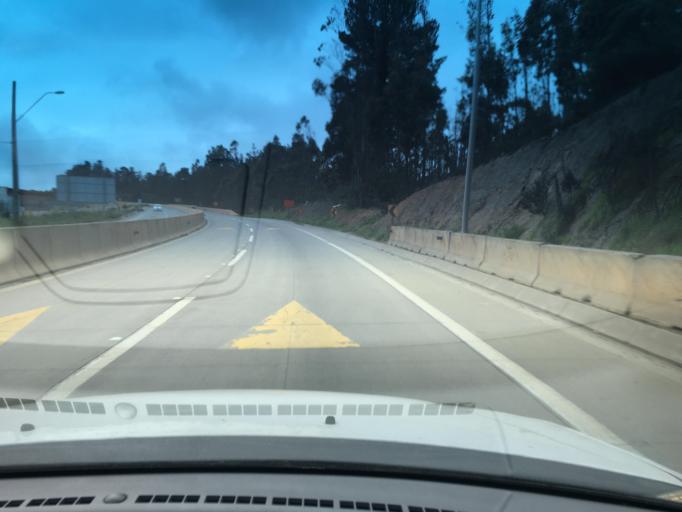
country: CL
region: Valparaiso
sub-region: Provincia de Valparaiso
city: Valparaiso
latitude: -33.0927
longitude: -71.6038
